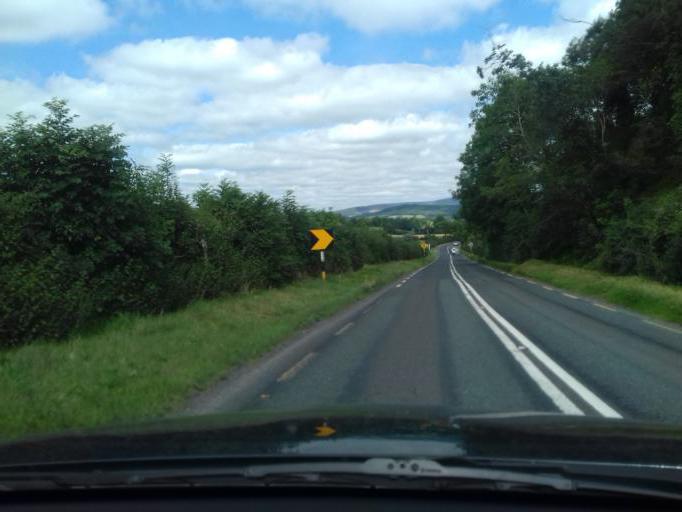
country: IE
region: Leinster
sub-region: Wicklow
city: Baltinglass
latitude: 52.9784
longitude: -6.6834
